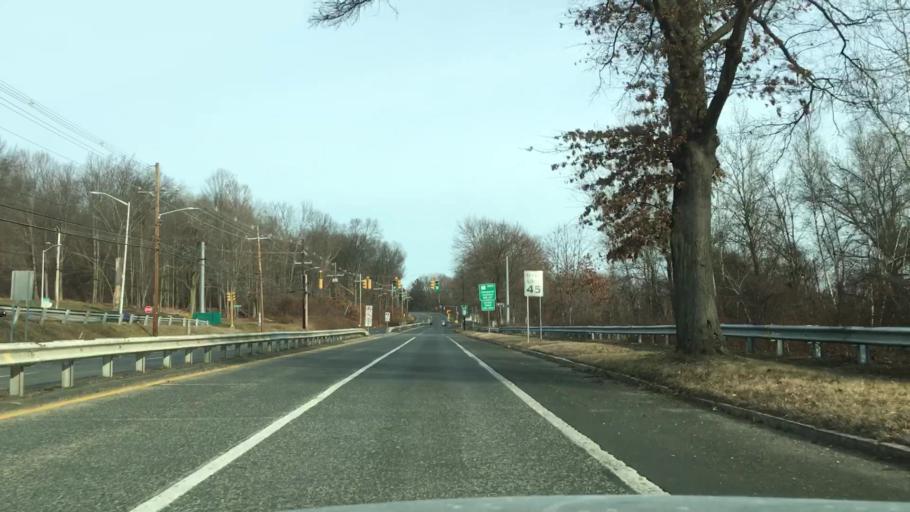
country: US
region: Massachusetts
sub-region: Hampden County
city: Chicopee
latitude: 42.1669
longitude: -72.6326
